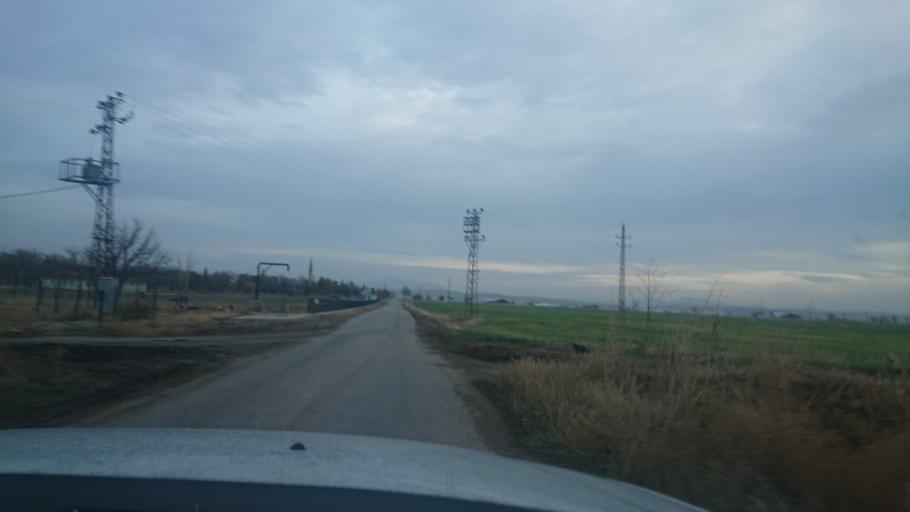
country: TR
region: Aksaray
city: Yesilova
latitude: 38.4545
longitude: 33.8380
